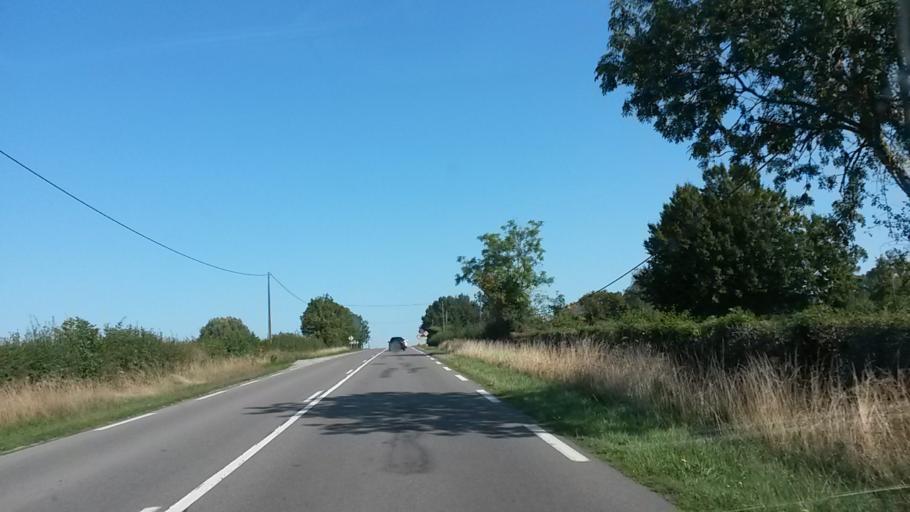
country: FR
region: Nord-Pas-de-Calais
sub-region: Departement du Nord
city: Avesnes-sur-Helpe
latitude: 50.1033
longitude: 3.9312
